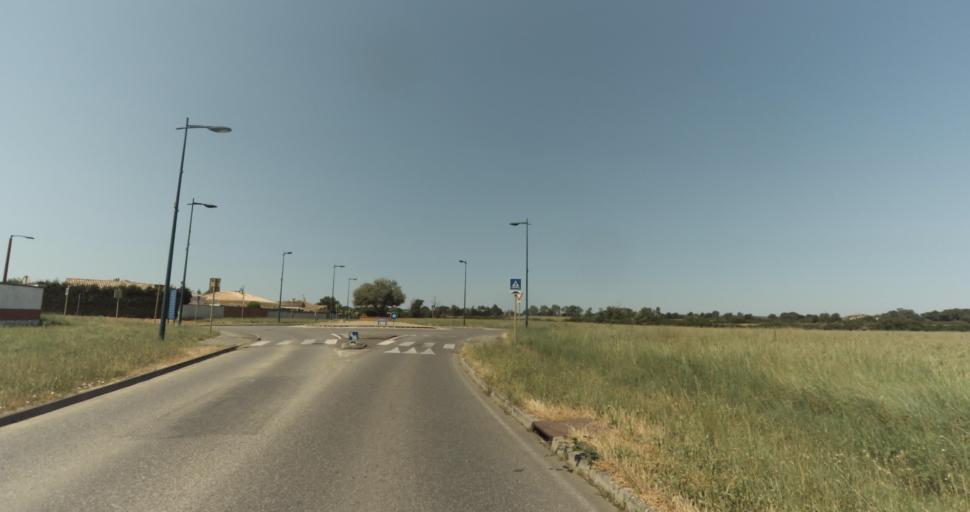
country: FR
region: Midi-Pyrenees
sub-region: Departement de la Haute-Garonne
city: La Salvetat-Saint-Gilles
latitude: 43.5748
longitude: 1.2451
